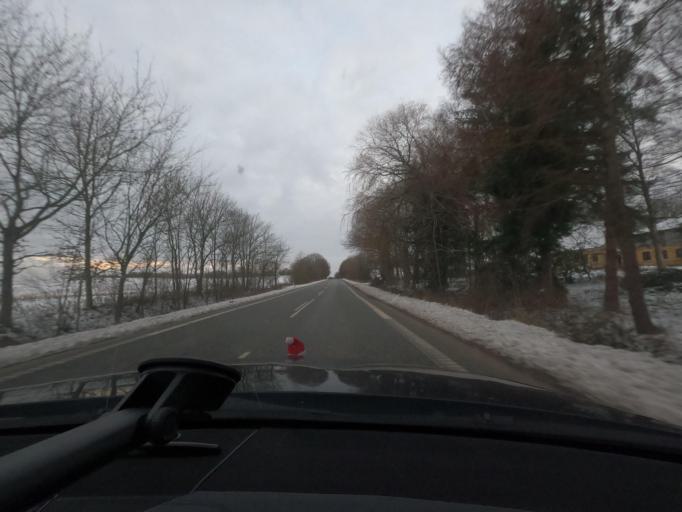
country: DE
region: Schleswig-Holstein
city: Glucksburg
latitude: 54.8894
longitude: 9.5210
